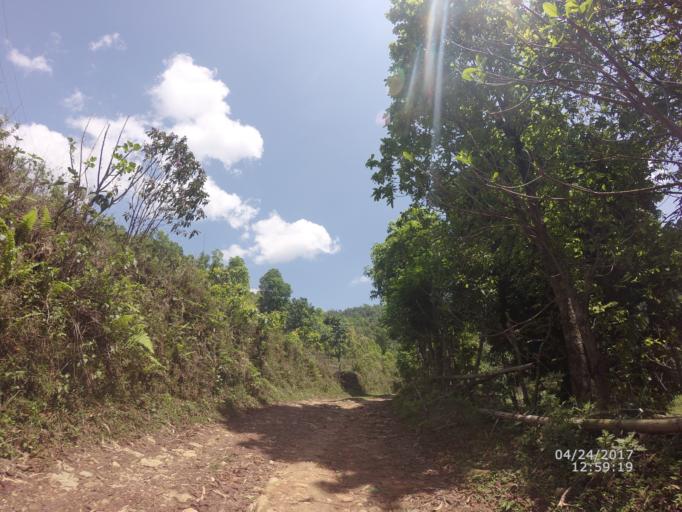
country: NP
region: Western Region
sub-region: Gandaki Zone
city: Pokhara
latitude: 28.1918
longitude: 84.0964
